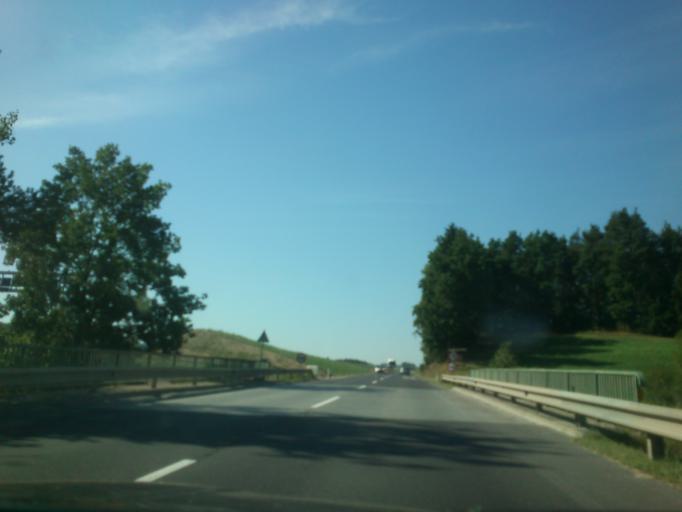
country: AT
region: Upper Austria
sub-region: Politischer Bezirk Freistadt
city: Freistadt
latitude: 48.4603
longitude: 14.5009
